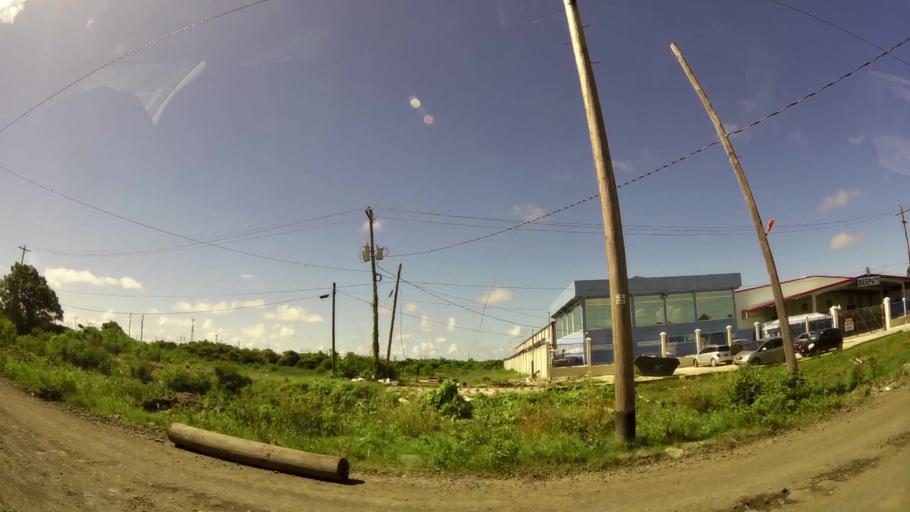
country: GY
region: Demerara-Mahaica
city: Georgetown
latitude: 6.8098
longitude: -58.1257
